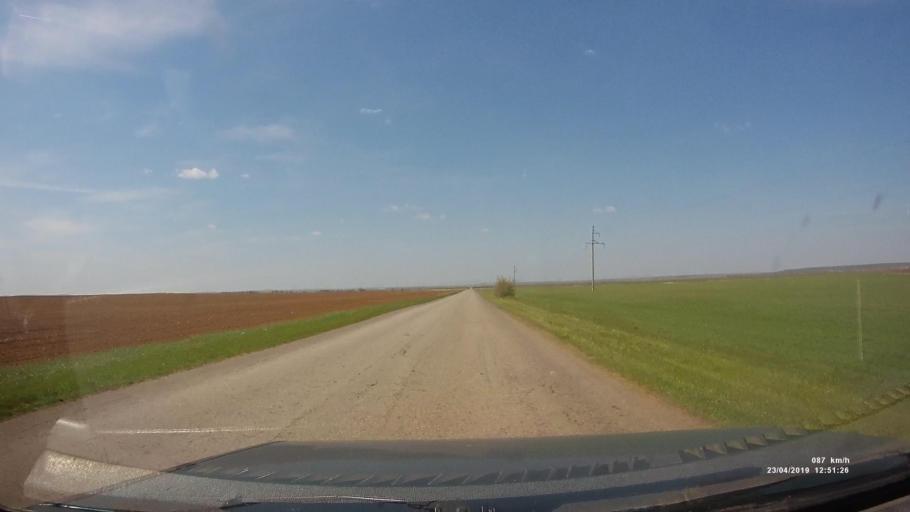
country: RU
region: Kalmykiya
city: Yashalta
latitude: 46.5549
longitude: 42.6227
